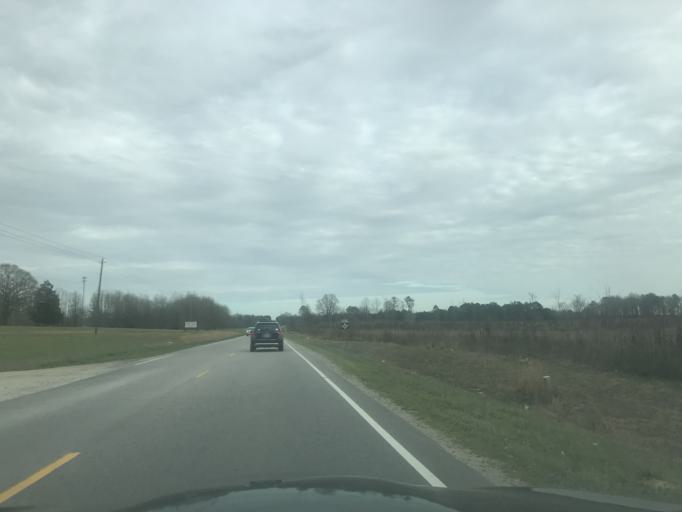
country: US
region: North Carolina
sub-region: Franklin County
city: Franklinton
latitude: 36.0931
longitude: -78.4048
